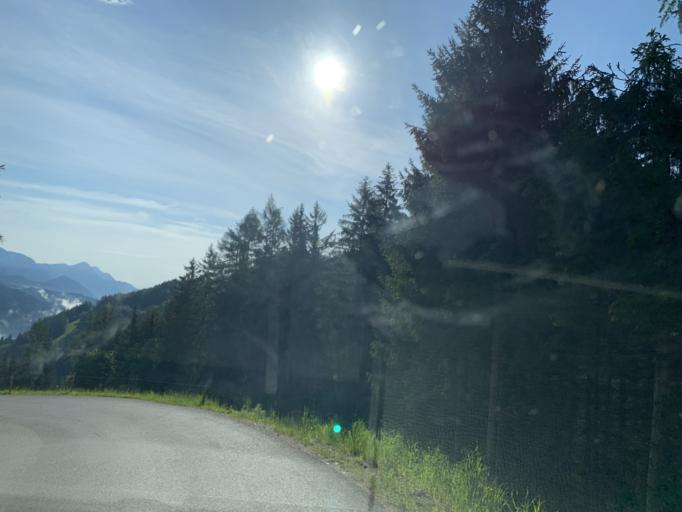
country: AT
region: Salzburg
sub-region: Politischer Bezirk Sankt Johann im Pongau
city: Forstau
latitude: 47.3754
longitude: 13.6103
